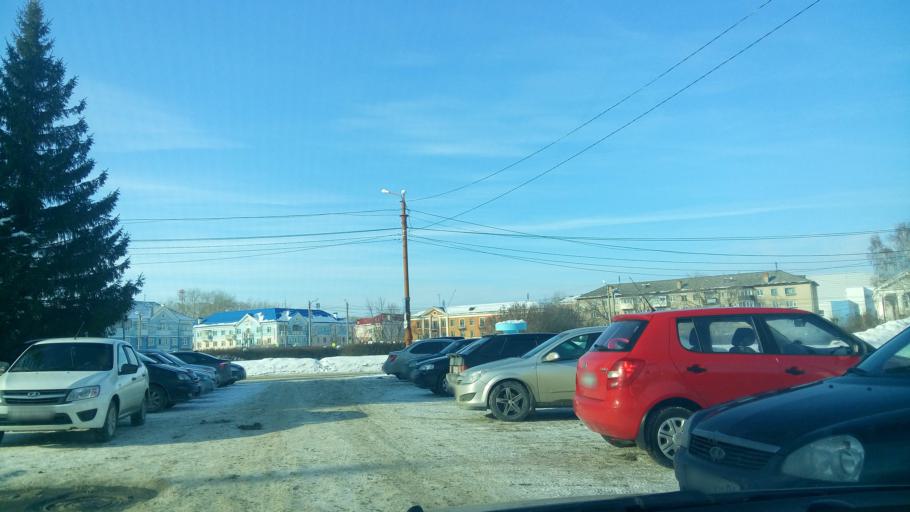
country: RU
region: Sverdlovsk
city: Bogdanovich
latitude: 56.7731
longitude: 62.0575
